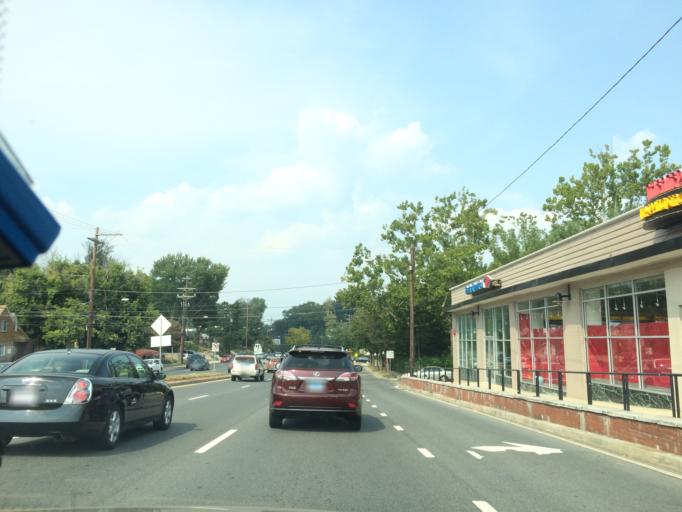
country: US
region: Maryland
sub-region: Montgomery County
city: Four Corners
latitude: 39.0210
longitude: -77.0121
